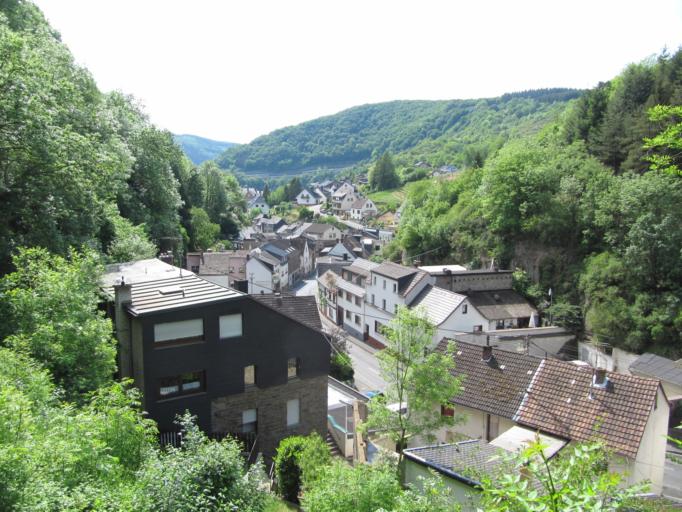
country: DE
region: Rheinland-Pfalz
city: Altenahr
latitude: 50.5192
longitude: 6.9957
